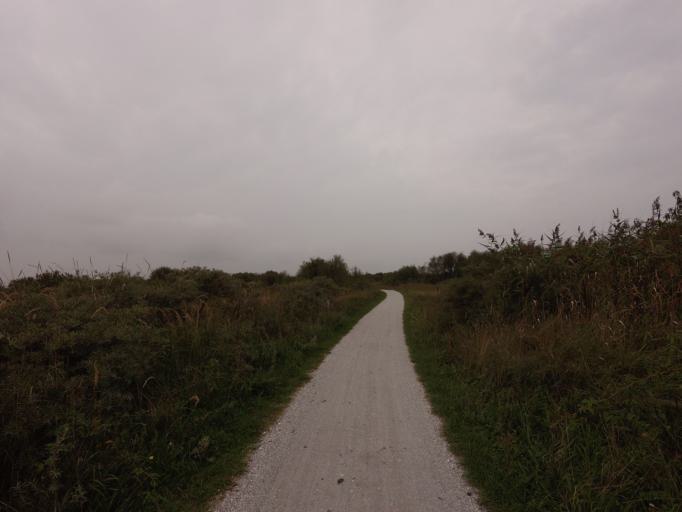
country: NL
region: Friesland
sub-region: Gemeente Schiermonnikoog
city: Schiermonnikoog
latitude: 53.4896
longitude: 6.2019
